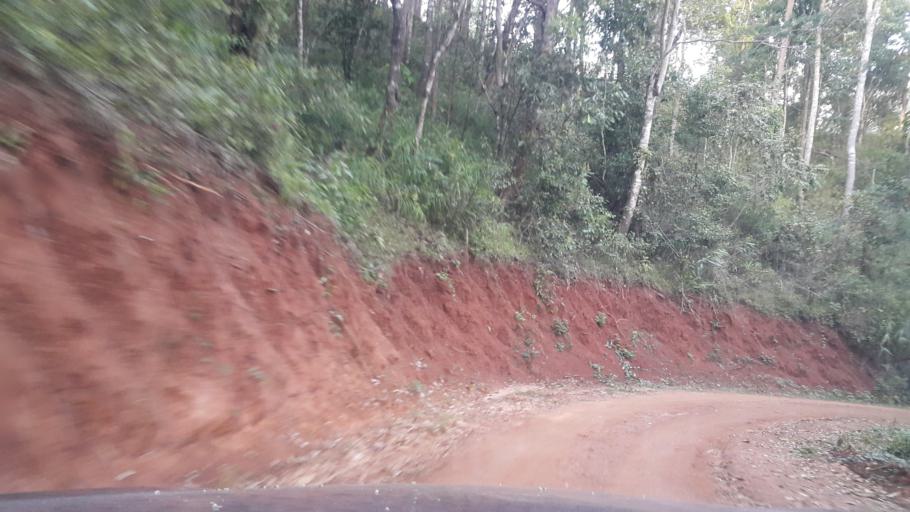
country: TH
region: Chiang Mai
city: Samoeng
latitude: 19.0074
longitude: 98.6616
